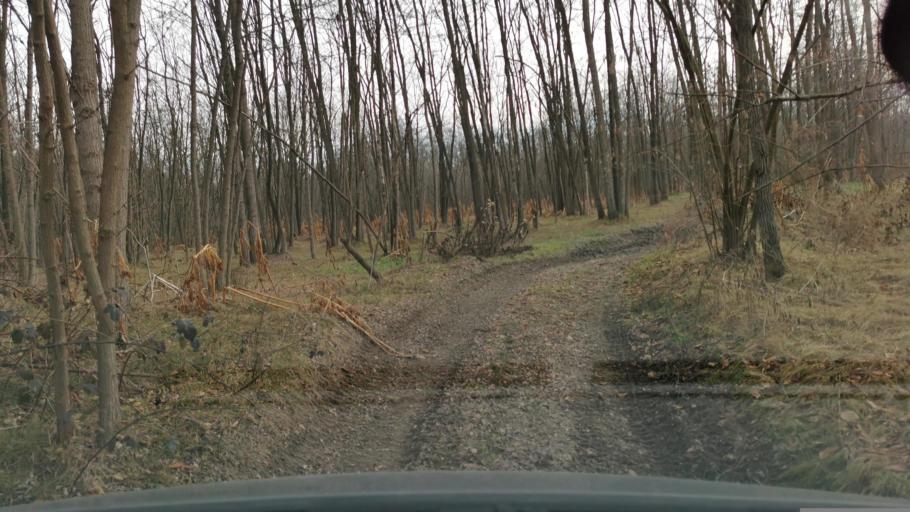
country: IT
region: Piedmont
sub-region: Provincia di Torino
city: San Benigno Canavese
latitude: 45.2520
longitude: 7.7982
